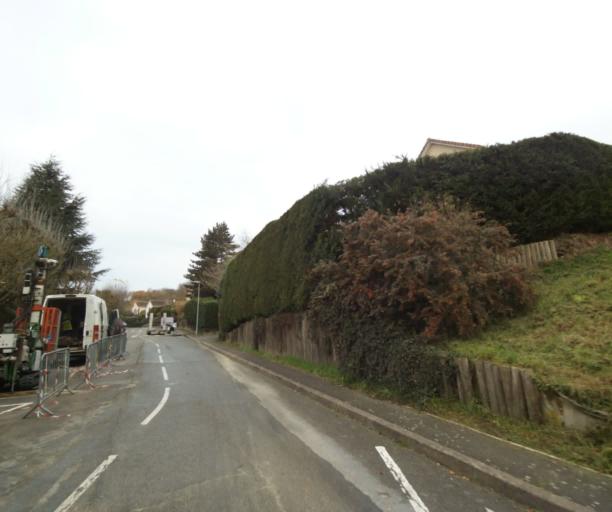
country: FR
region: Ile-de-France
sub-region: Departement des Yvelines
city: Triel-sur-Seine
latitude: 48.9821
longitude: 2.0174
